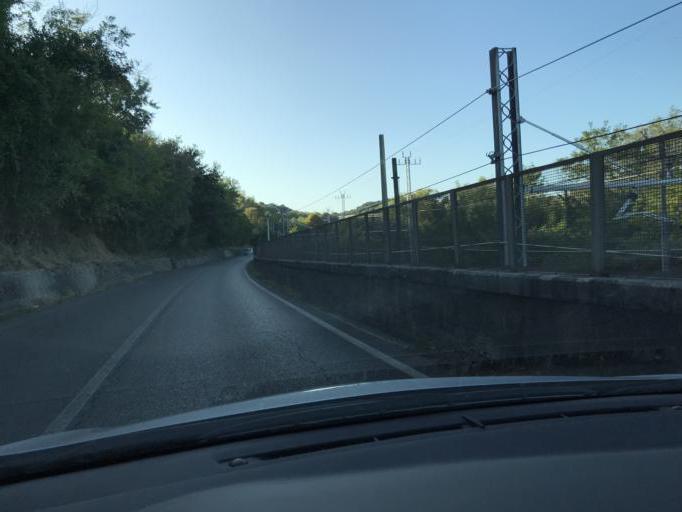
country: IT
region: Latium
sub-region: Provincia di Viterbo
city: Orte
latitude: 42.4466
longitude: 12.3945
